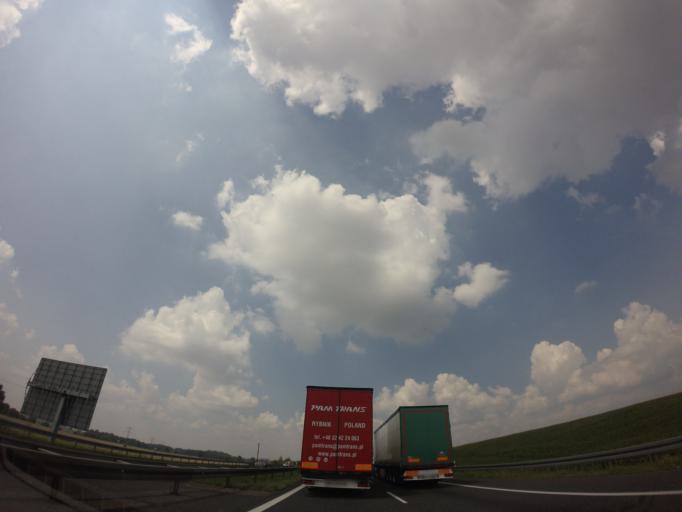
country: PL
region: Silesian Voivodeship
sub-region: Powiat gliwicki
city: Rudziniec
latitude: 50.3964
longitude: 18.4381
